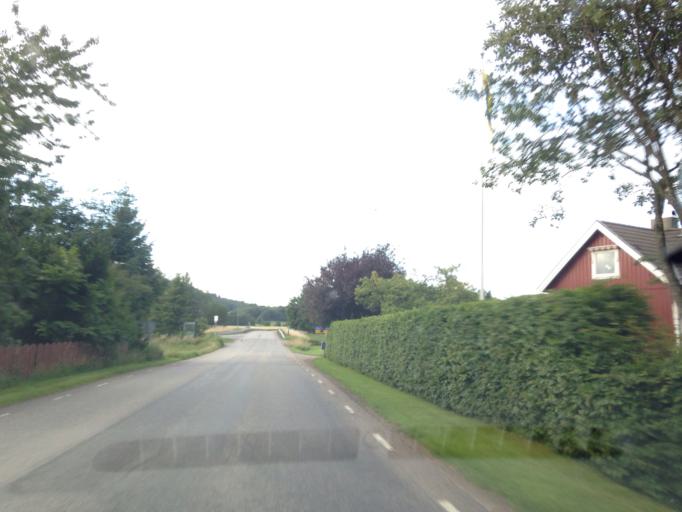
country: SE
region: Halland
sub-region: Varbergs Kommun
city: Tvaaker
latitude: 57.1334
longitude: 12.4555
